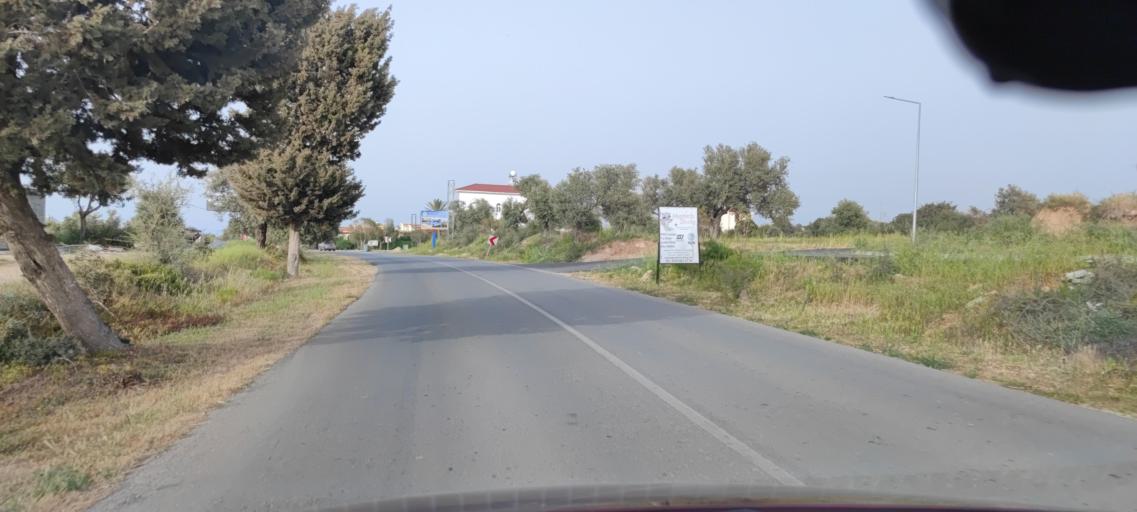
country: CY
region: Ammochostos
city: Leonarisso
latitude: 35.5446
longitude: 34.2005
